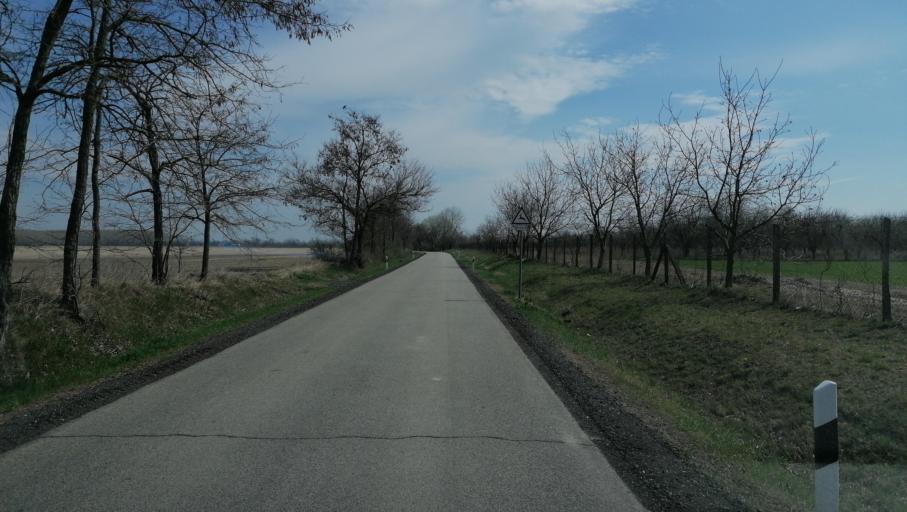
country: HU
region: Pest
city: Kiskunlachaza
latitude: 47.1914
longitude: 18.9745
